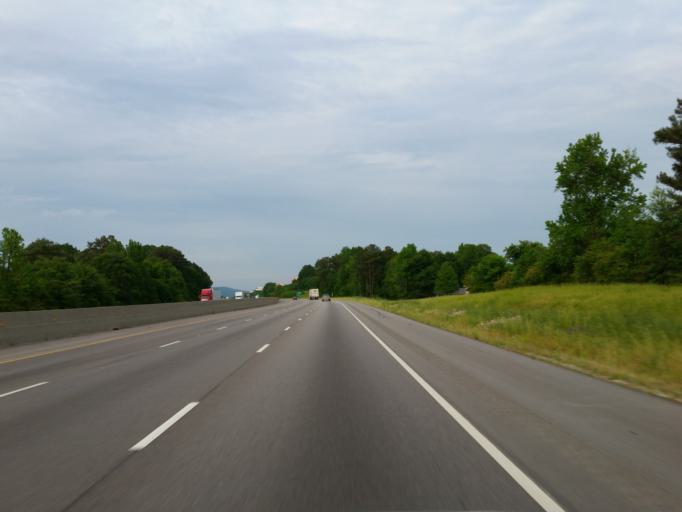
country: US
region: Alabama
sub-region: Calhoun County
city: Oxford
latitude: 33.5938
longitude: -85.8580
